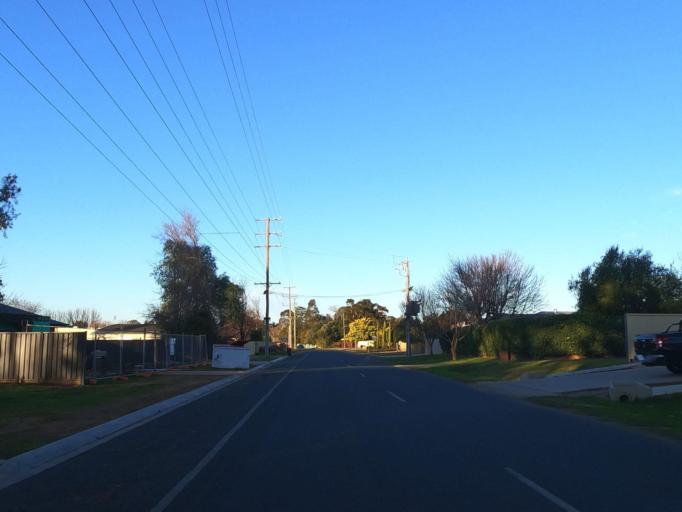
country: AU
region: Victoria
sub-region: Swan Hill
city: Swan Hill
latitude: -35.3603
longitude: 143.5548
